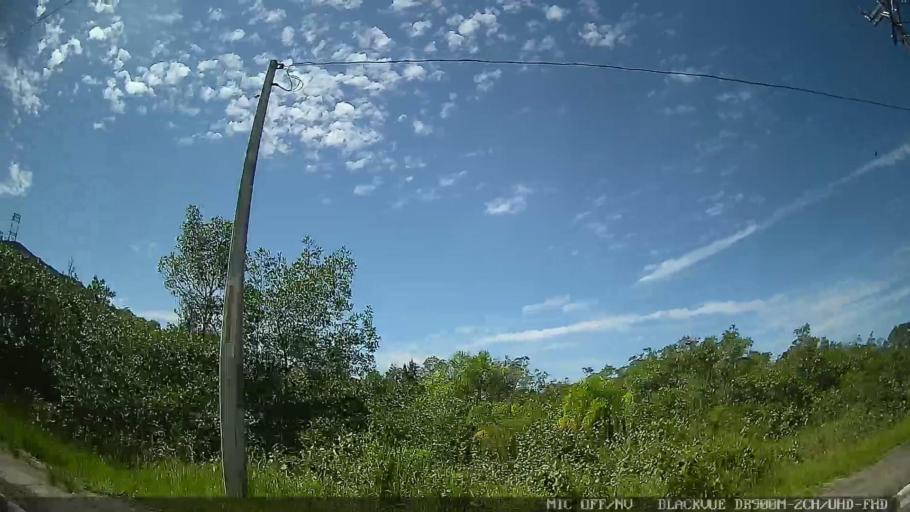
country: BR
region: Sao Paulo
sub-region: Iguape
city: Iguape
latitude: -24.7095
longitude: -47.5430
